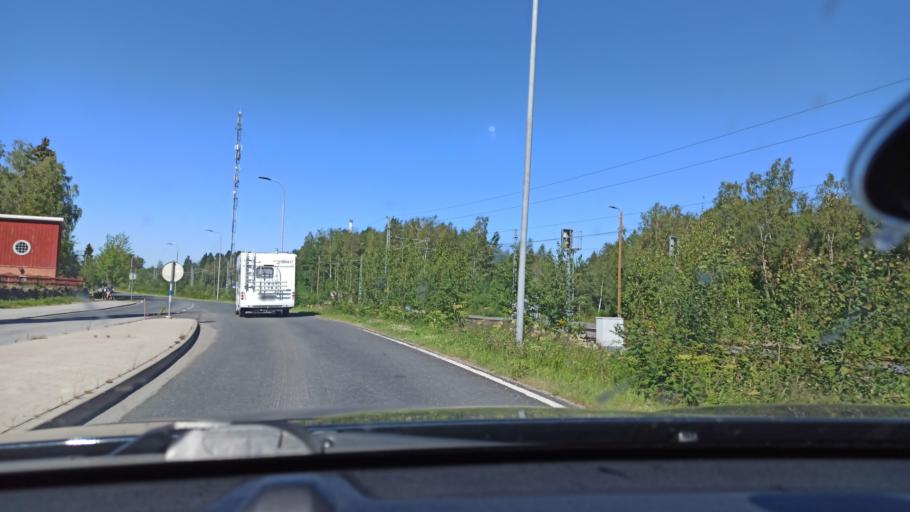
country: FI
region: Ostrobothnia
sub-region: Jakobstadsregionen
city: Jakobstad
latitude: 63.6696
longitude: 22.7143
